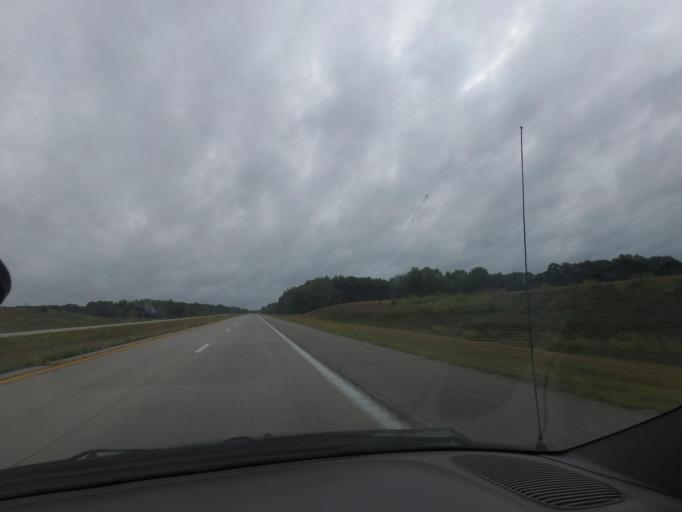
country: US
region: Missouri
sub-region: Shelby County
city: Shelbina
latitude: 39.6711
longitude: -91.8963
